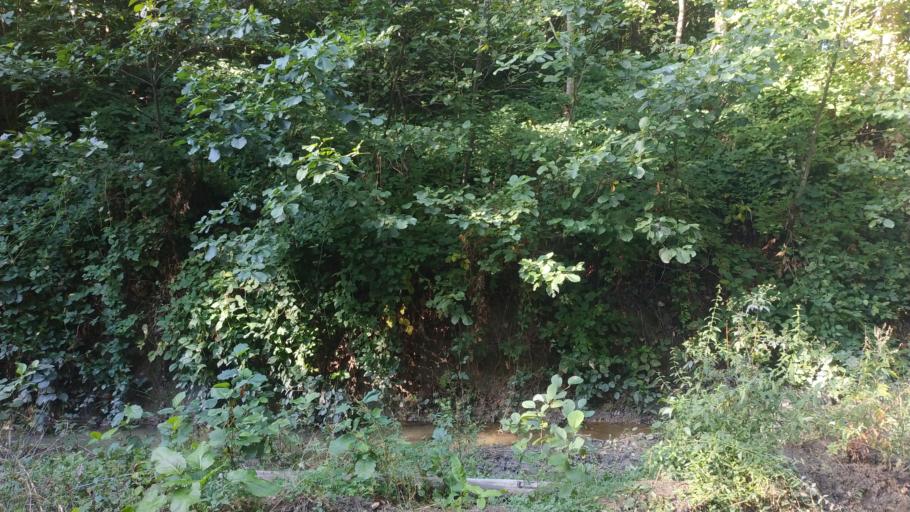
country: RU
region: Krasnodarskiy
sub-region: Sochi City
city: Lazarevskoye
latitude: 43.9884
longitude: 39.3963
